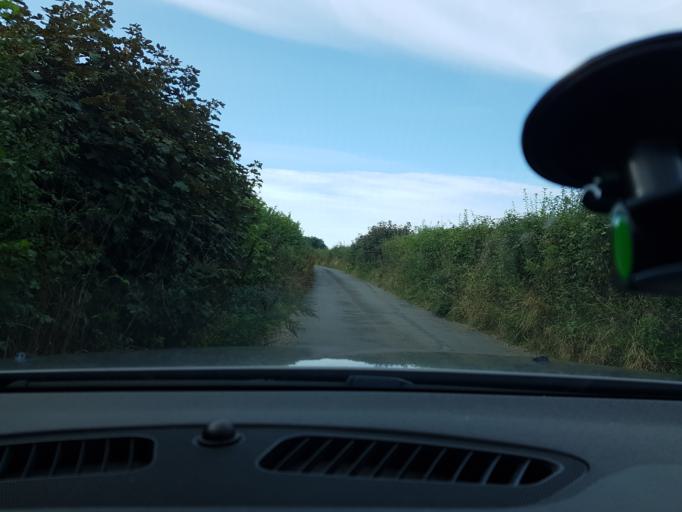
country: GB
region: England
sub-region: West Berkshire
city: Hungerford
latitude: 51.3935
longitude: -1.4948
